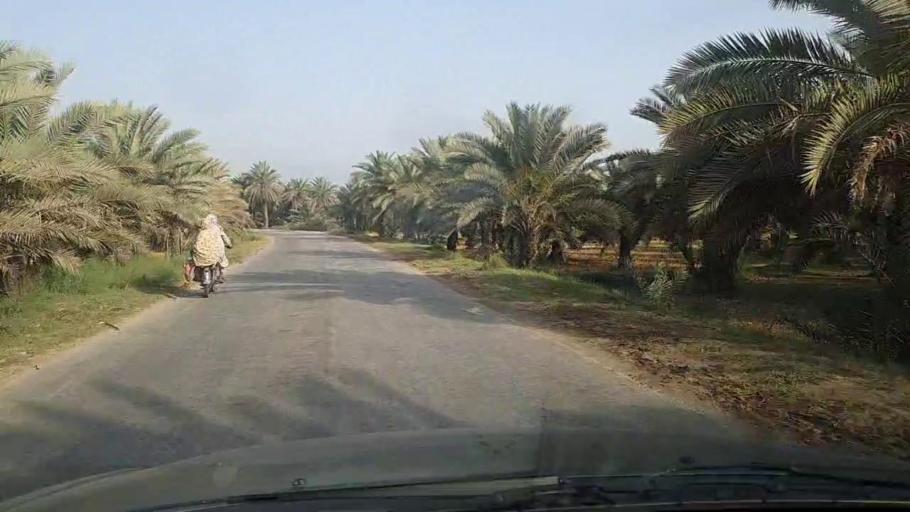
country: PK
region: Sindh
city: Pir jo Goth
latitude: 27.5675
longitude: 68.6411
